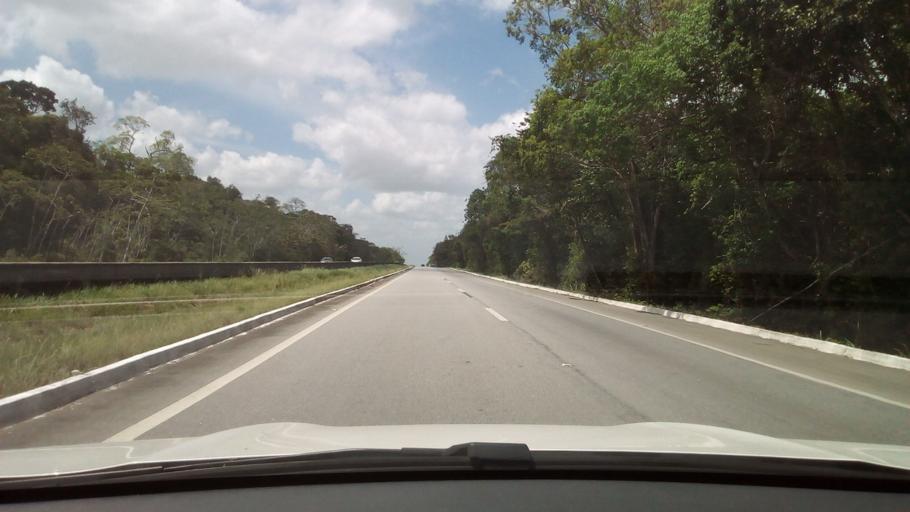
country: BR
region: Paraiba
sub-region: Mamanguape
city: Mamanguape
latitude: -6.9771
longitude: -35.0781
